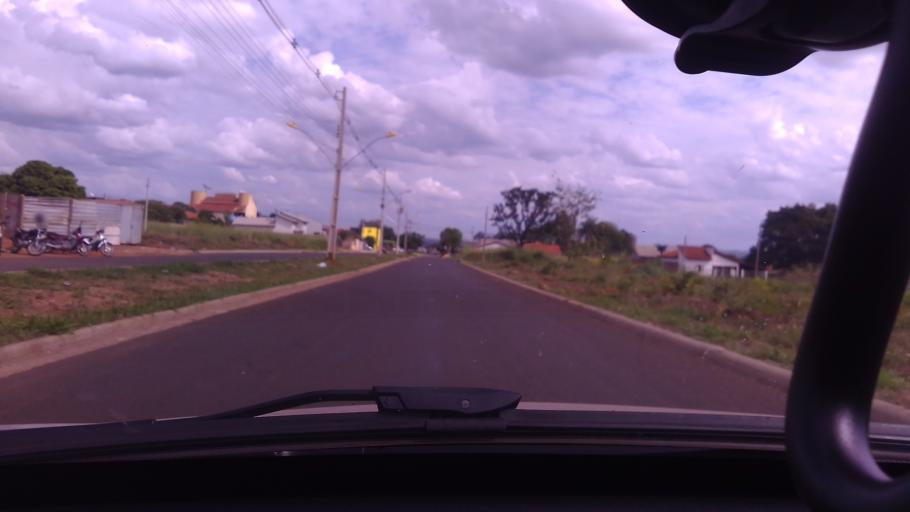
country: BR
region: Goias
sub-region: Mineiros
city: Mineiros
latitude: -17.5775
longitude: -52.5544
